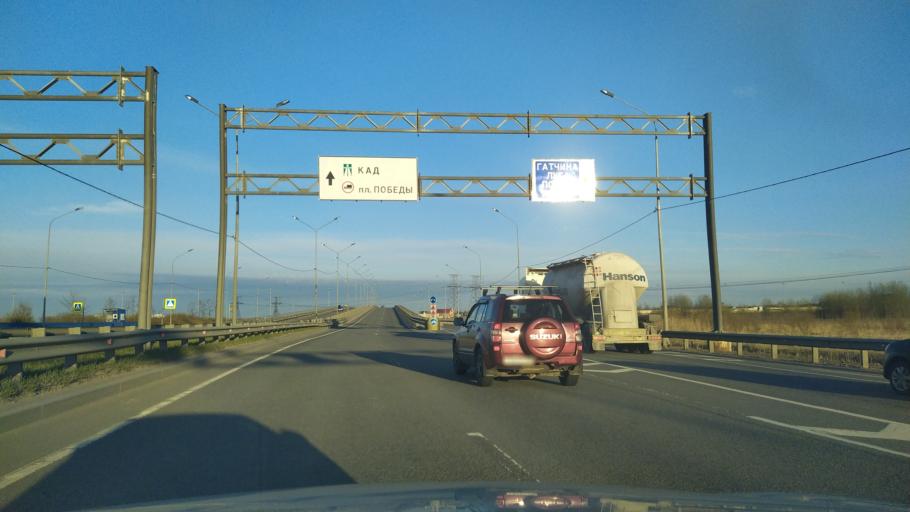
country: RU
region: St.-Petersburg
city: Aleksandrovskaya
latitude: 59.7467
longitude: 30.3036
